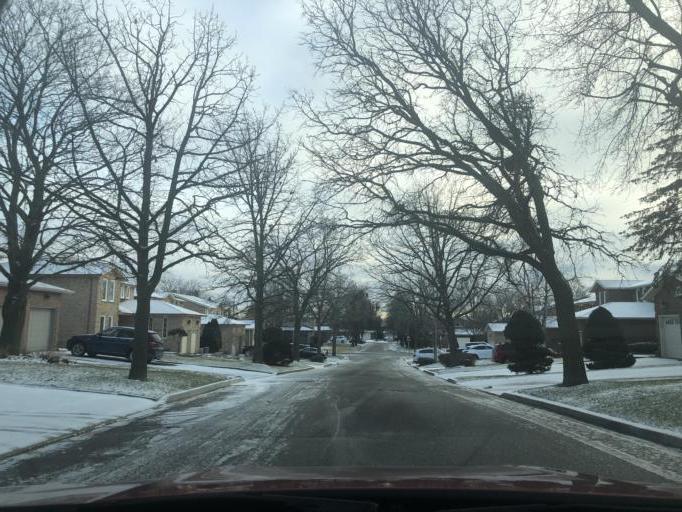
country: CA
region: Ontario
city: Markham
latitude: 43.8741
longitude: -79.2397
